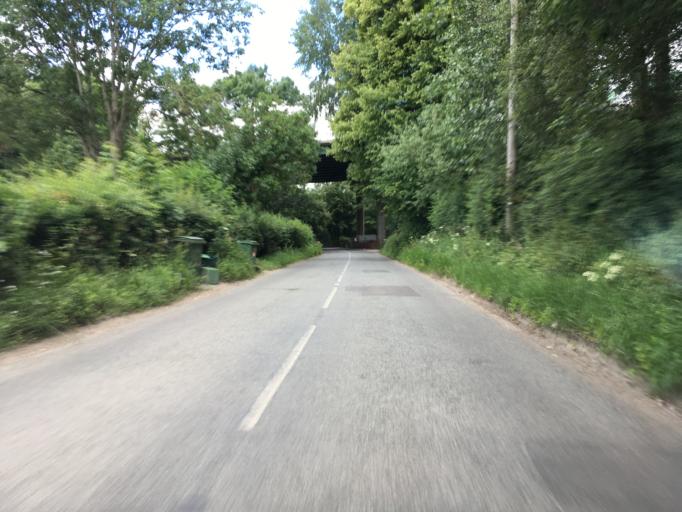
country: GB
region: England
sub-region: West Berkshire
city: Welford
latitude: 51.4499
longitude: -1.4046
